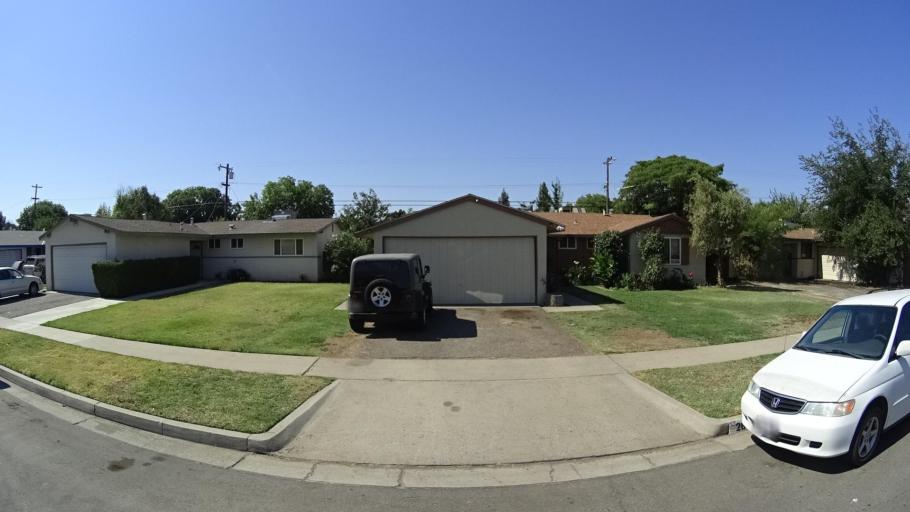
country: US
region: California
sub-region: Fresno County
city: Fresno
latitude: 36.7956
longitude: -119.7779
